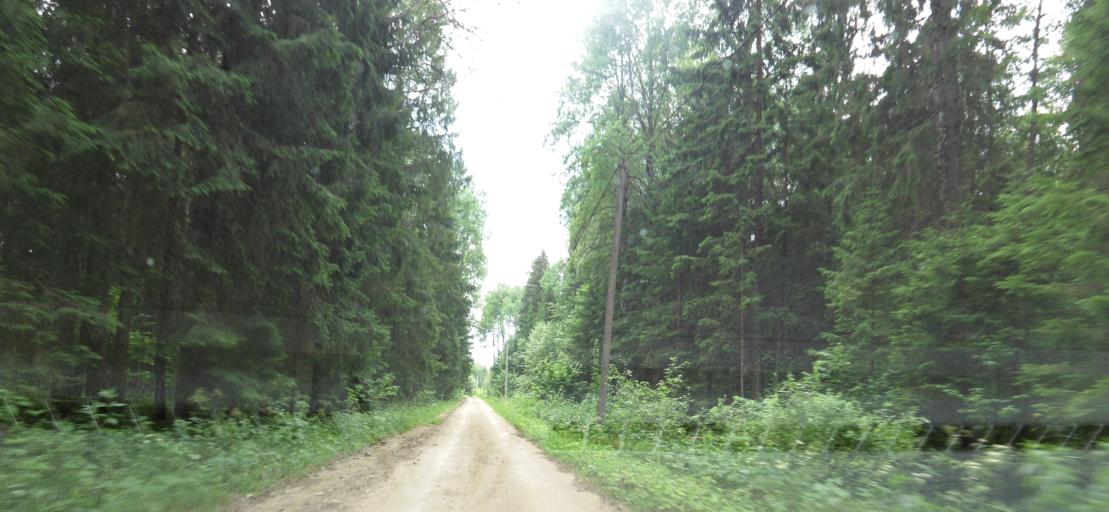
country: LV
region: Ogre
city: Jumprava
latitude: 56.4383
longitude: 24.9041
